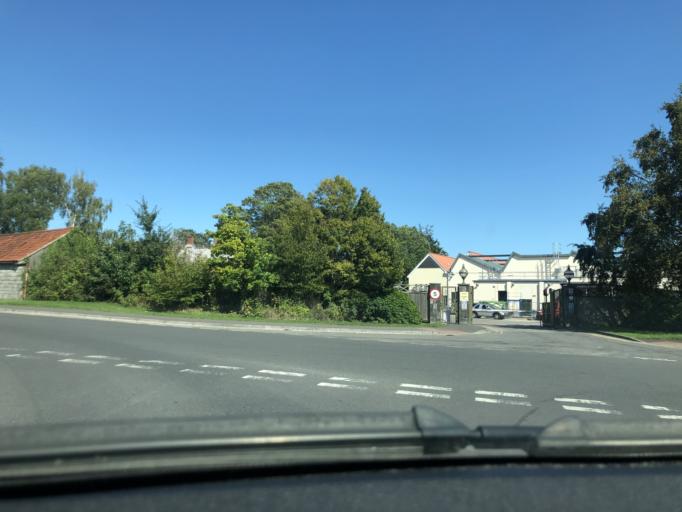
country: GB
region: England
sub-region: Somerset
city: Street
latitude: 51.1287
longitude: -2.7426
